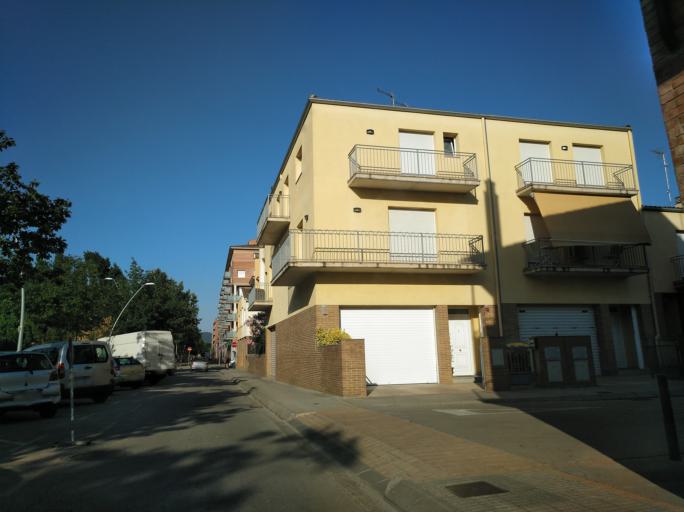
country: ES
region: Catalonia
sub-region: Provincia de Girona
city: Salt
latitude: 41.9704
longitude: 2.7898
